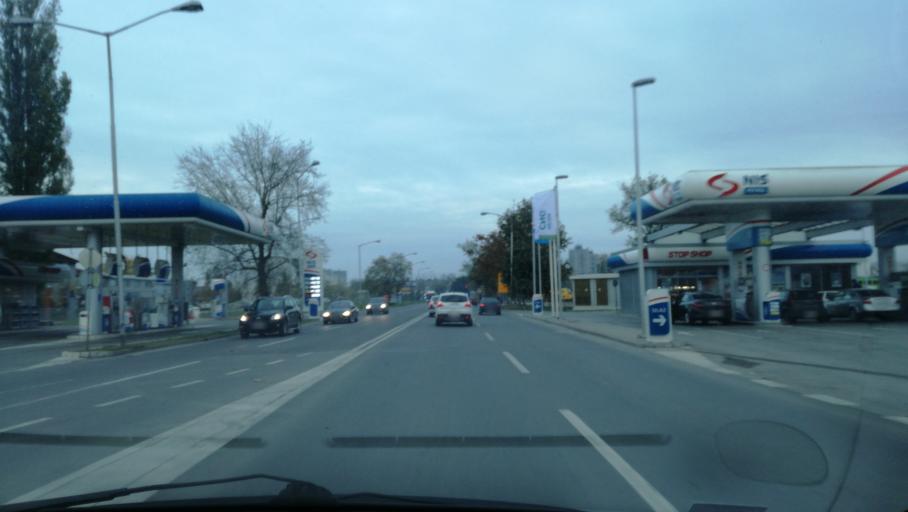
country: RS
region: Autonomna Pokrajina Vojvodina
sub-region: Juznobacki Okrug
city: Novi Sad
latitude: 45.2726
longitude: 19.8305
